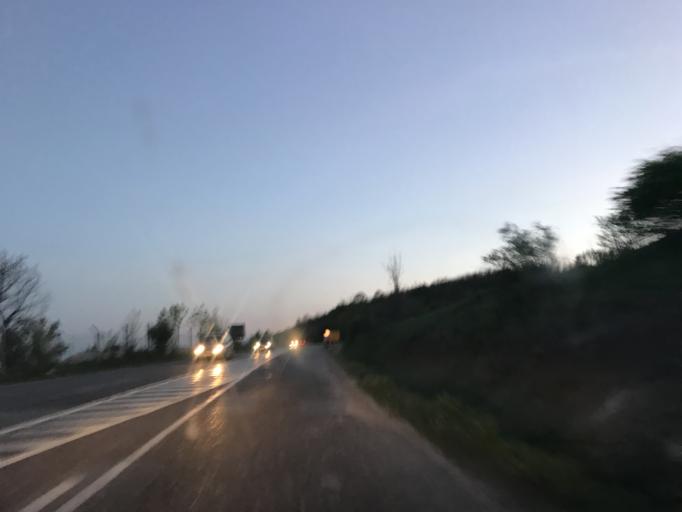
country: RS
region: Central Serbia
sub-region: Zajecarski Okrug
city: Zajecar
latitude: 43.9425
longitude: 22.3089
